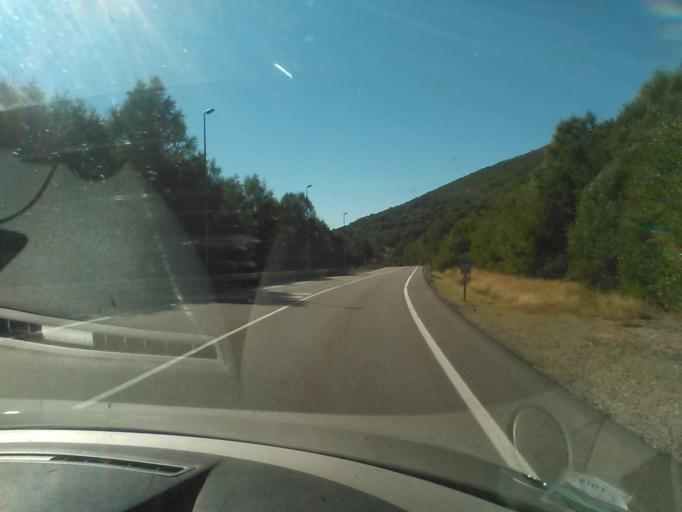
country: ES
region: Castille and Leon
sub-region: Provincia de Zamora
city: Lubian
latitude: 42.0336
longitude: -6.8389
